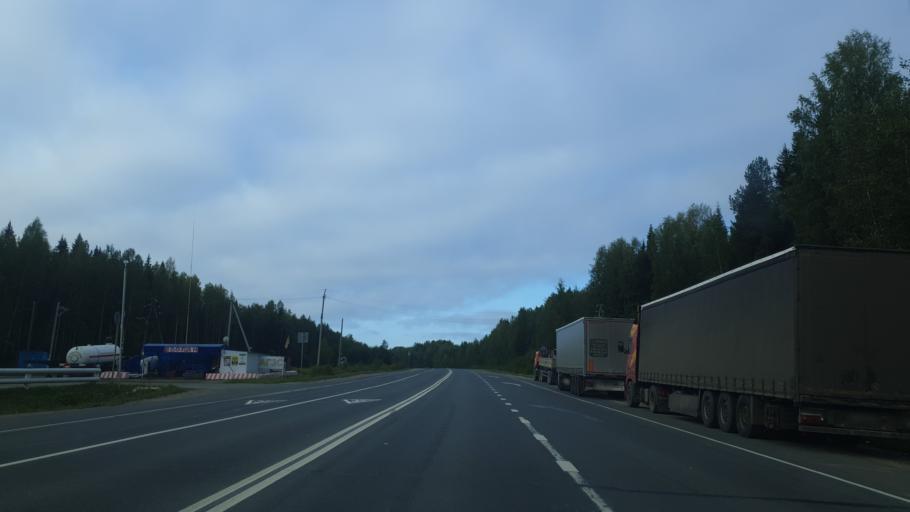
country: RU
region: Komi Republic
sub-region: Syktyvdinskiy Rayon
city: Syktyvkar
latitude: 61.5739
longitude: 50.6535
